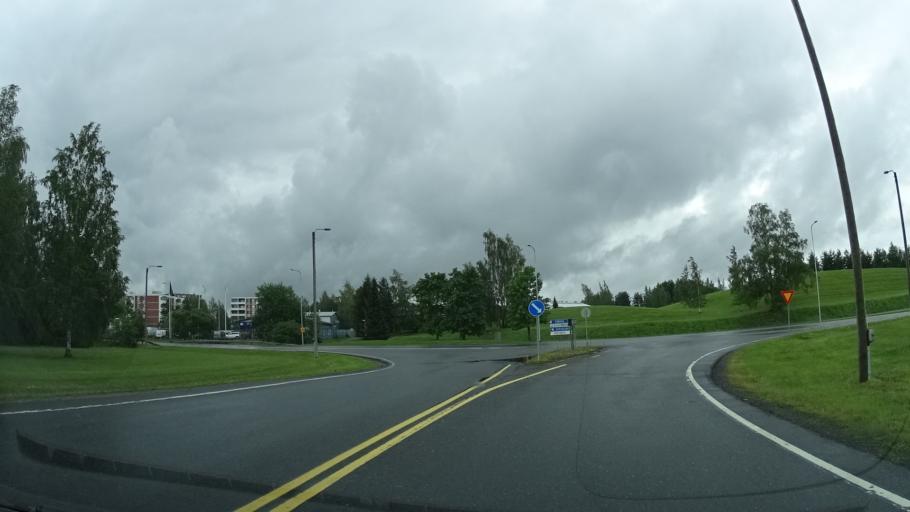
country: FI
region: Haeme
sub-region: Forssa
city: Forssa
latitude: 60.8096
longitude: 23.6063
